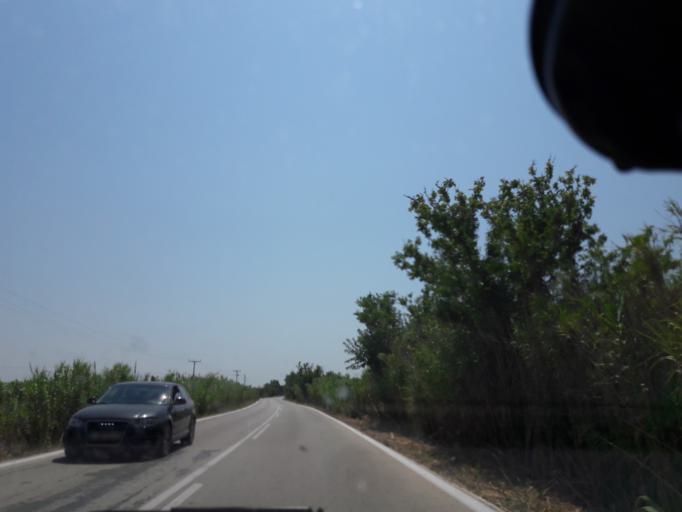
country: GR
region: North Aegean
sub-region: Nomos Lesvou
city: Myrina
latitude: 39.9342
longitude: 25.3426
